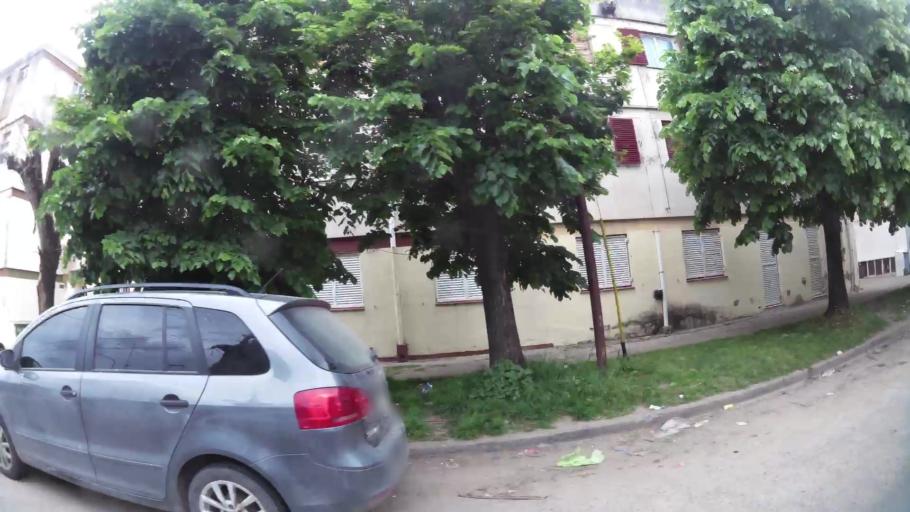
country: AR
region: Buenos Aires
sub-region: Partido de Zarate
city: Zarate
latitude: -34.1149
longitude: -59.0150
